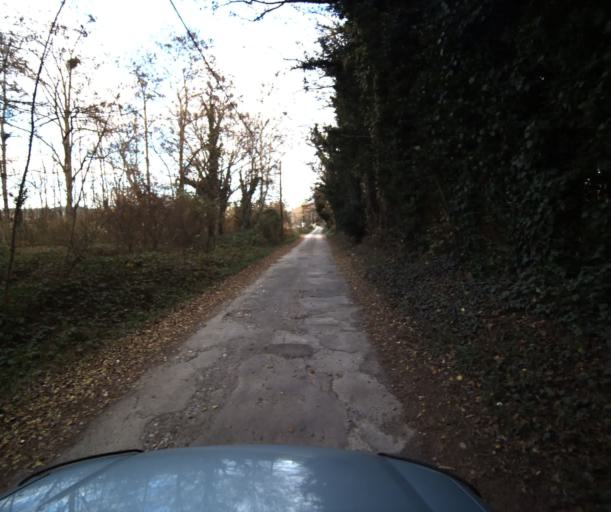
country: FR
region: Provence-Alpes-Cote d'Azur
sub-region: Departement des Bouches-du-Rhone
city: Meyrargues
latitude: 43.6665
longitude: 5.5255
